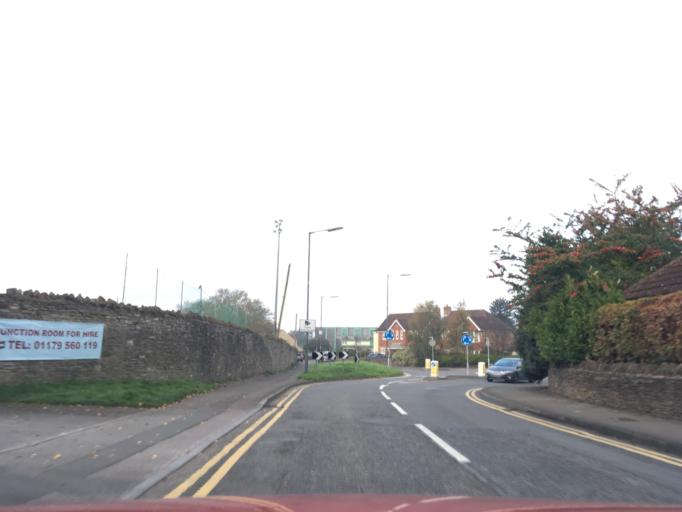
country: GB
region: England
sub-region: South Gloucestershire
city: Mangotsfield
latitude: 51.4832
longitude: -2.4804
